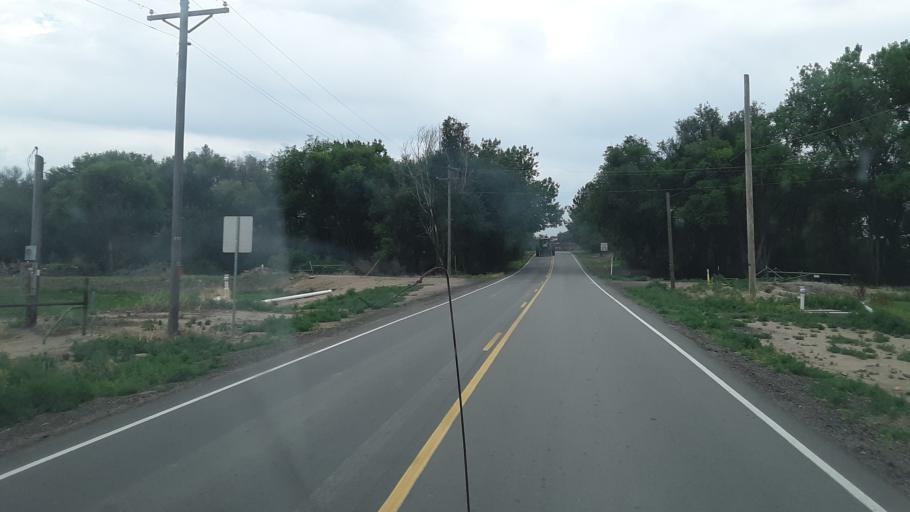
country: US
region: Colorado
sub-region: Otero County
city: Fowler
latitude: 38.1353
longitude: -104.0226
